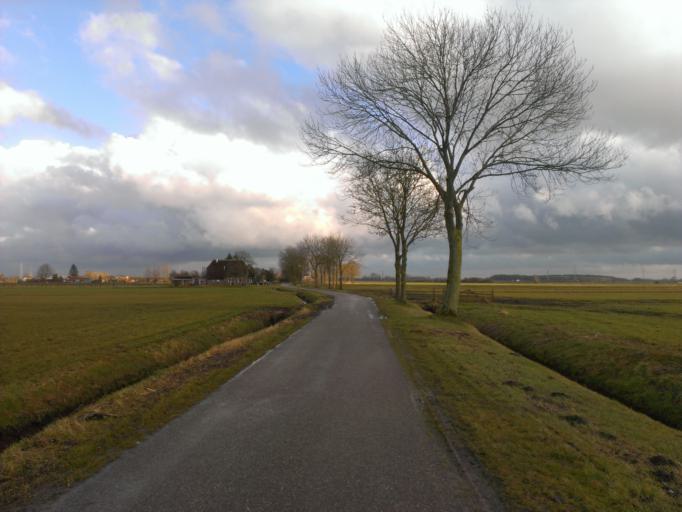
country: NL
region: Gelderland
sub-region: Gemeente Heerde
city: Heerde
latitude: 52.3860
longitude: 6.0578
